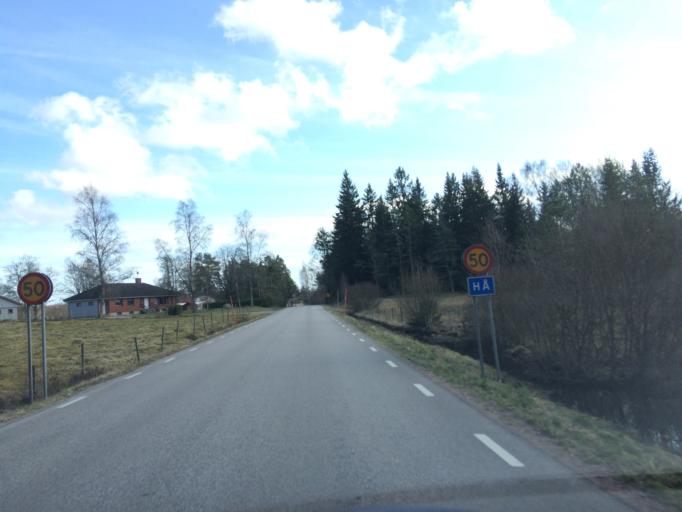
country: SE
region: Kronoberg
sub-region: Ljungby Kommun
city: Ljungby
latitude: 56.6659
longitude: 13.9030
